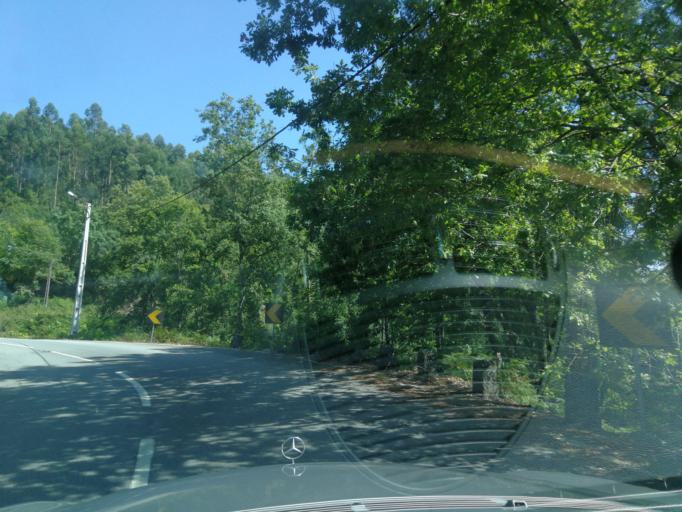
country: PT
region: Braga
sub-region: Braga
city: Adaufe
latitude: 41.5786
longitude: -8.3887
